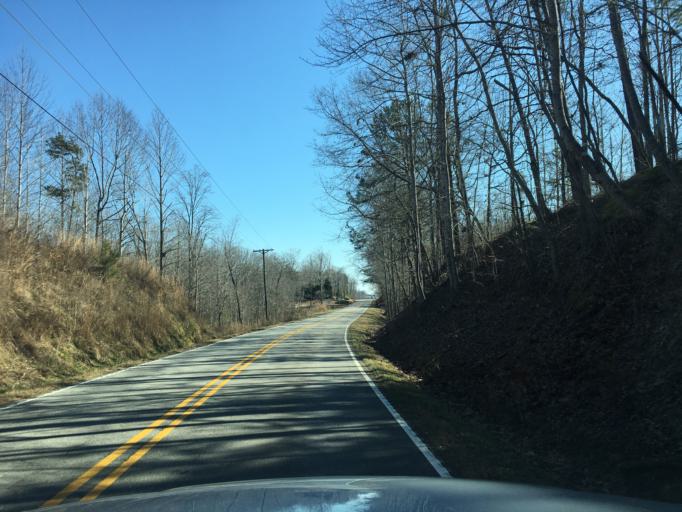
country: US
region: South Carolina
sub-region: Pickens County
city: Liberty
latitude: 34.8059
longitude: -82.7624
